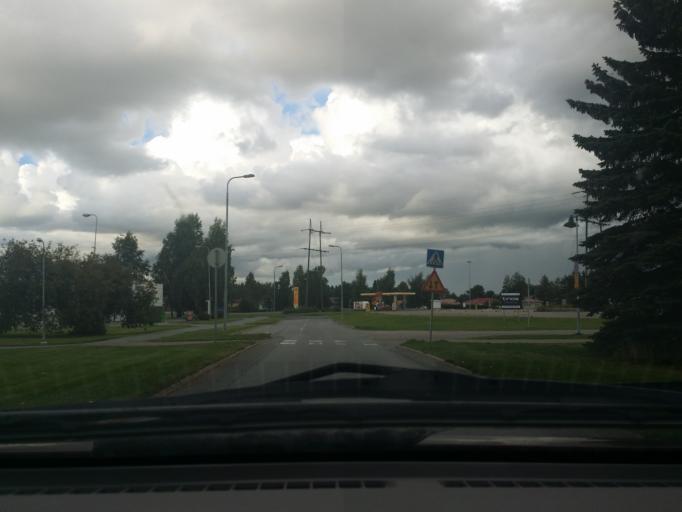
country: FI
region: Satakunta
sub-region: Pori
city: Pori
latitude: 61.4969
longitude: 21.8053
